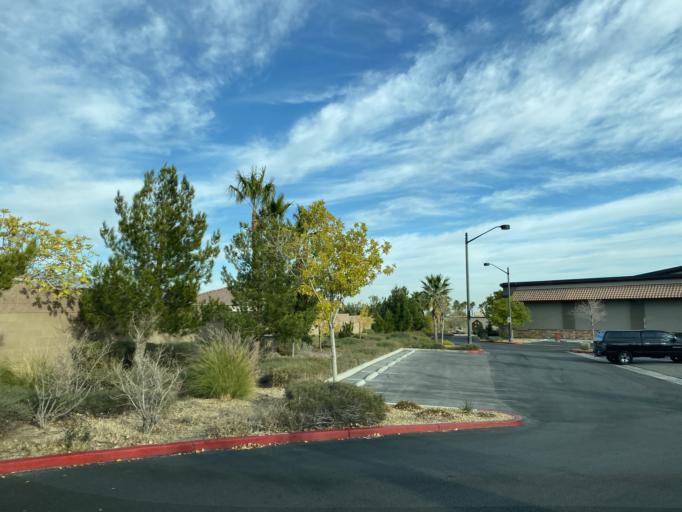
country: US
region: Nevada
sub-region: Clark County
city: Summerlin South
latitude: 36.3027
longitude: -115.2841
